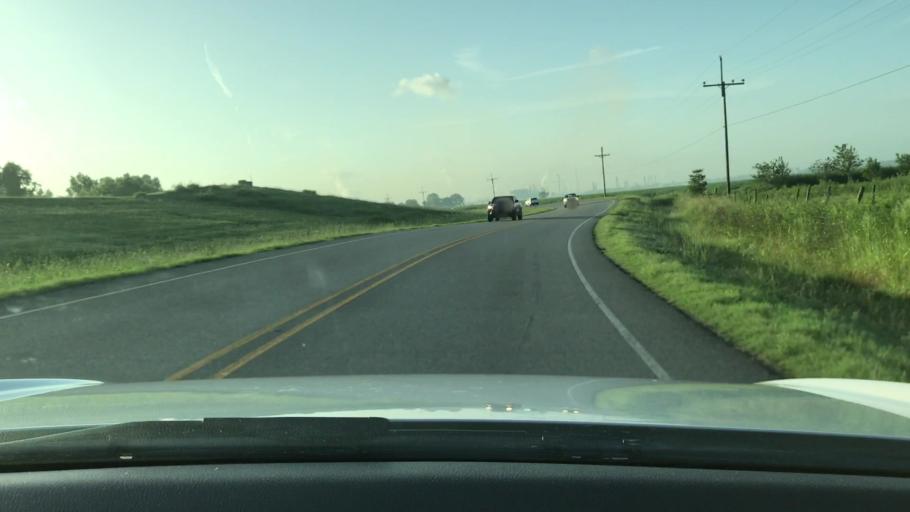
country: US
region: Louisiana
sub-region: Iberville Parish
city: Plaquemine
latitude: 30.2754
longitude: -91.2088
